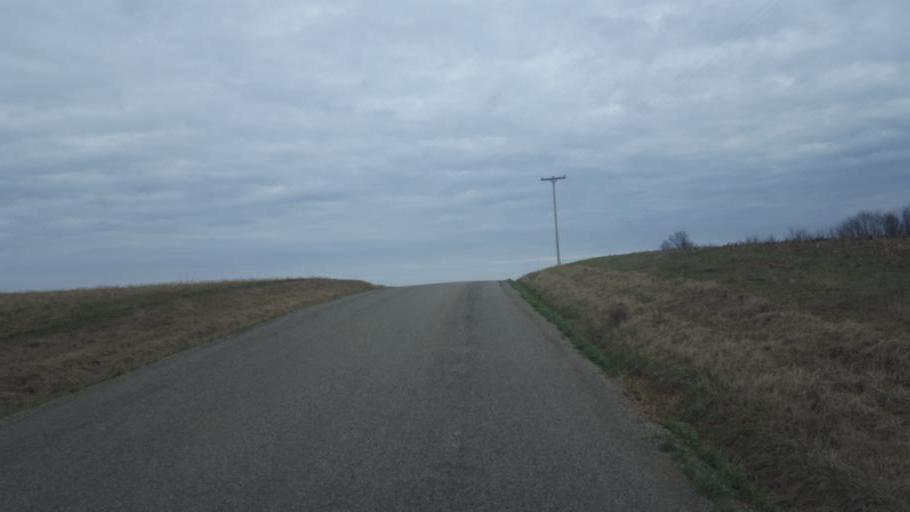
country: US
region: Ohio
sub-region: Knox County
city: Danville
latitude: 40.5312
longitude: -82.3800
